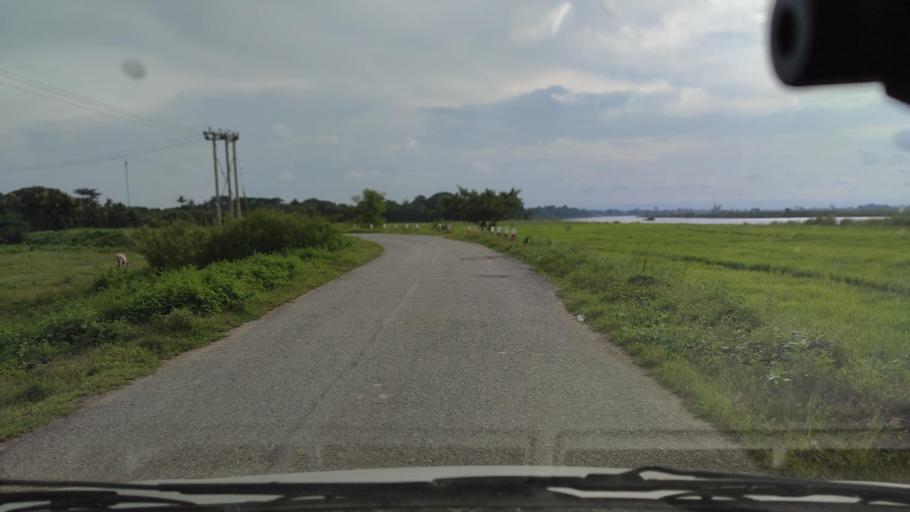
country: MM
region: Bago
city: Pyu
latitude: 18.5541
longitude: 96.5872
